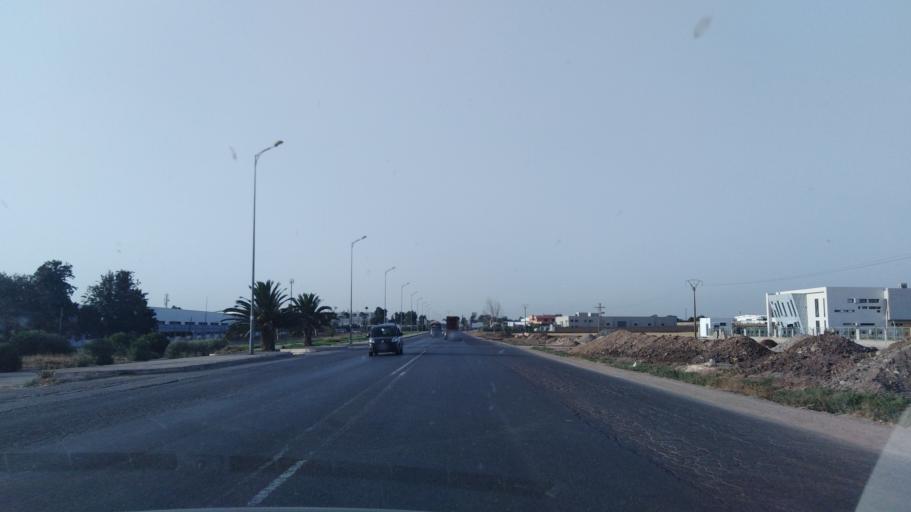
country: MA
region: Chaouia-Ouardigha
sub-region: Settat Province
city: Berrechid
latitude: 33.2405
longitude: -7.5876
